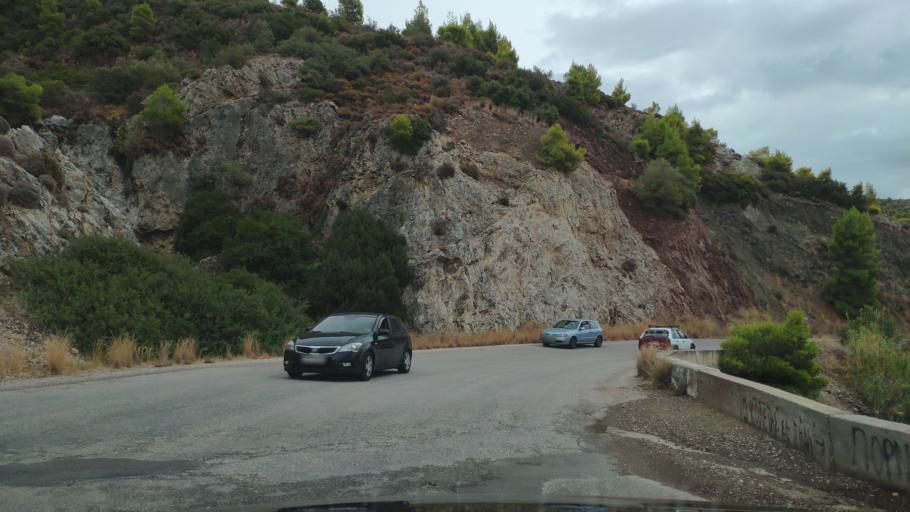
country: GR
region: Peloponnese
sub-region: Nomos Korinthias
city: Perachora
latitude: 38.0008
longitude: 22.9456
